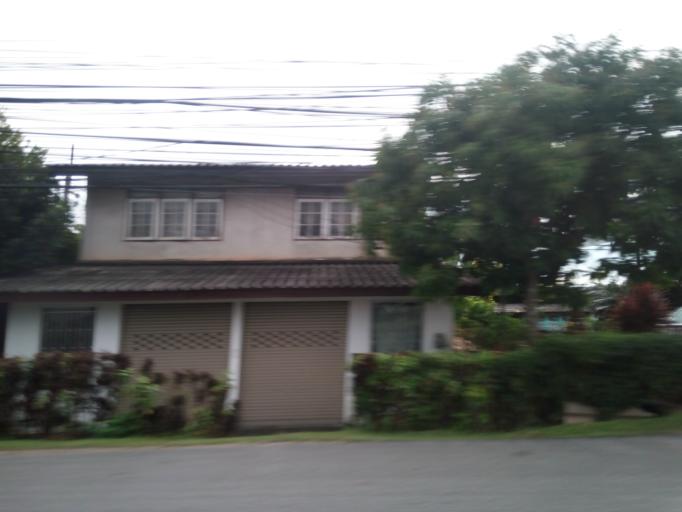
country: TH
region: Phuket
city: Thalang
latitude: 7.9953
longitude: 98.3519
